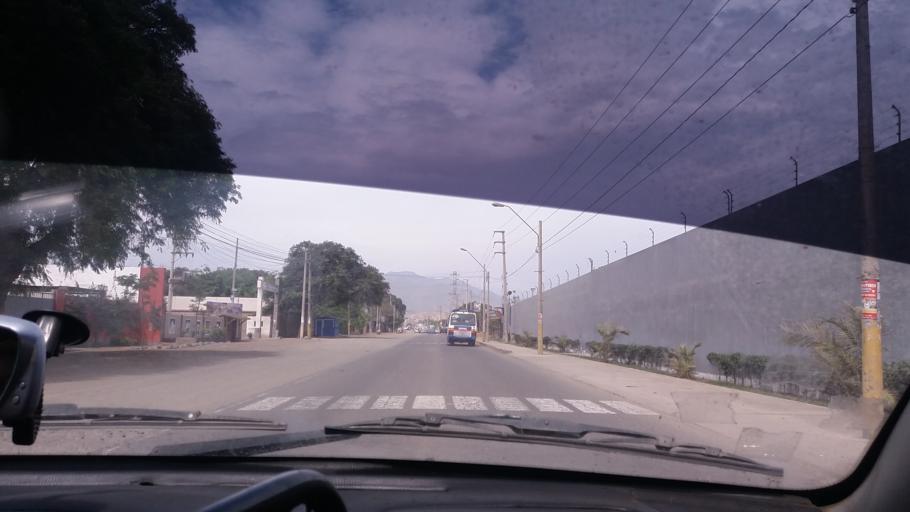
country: PE
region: Lima
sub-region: Lima
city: Punta Hermosa
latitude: -12.2550
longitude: -76.8786
